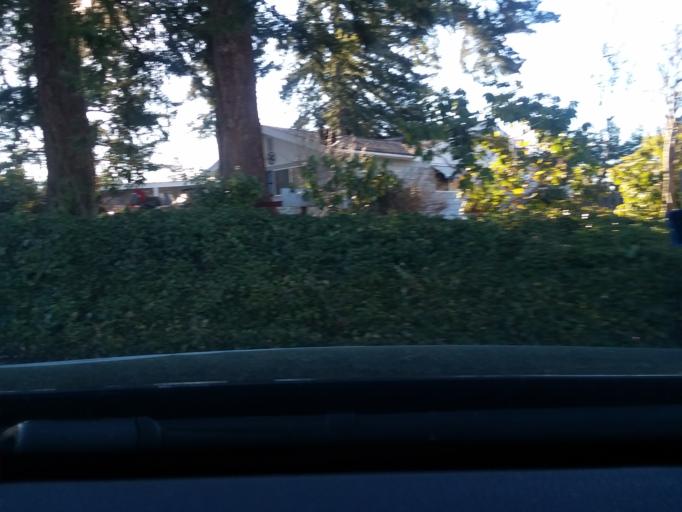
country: US
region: Washington
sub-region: Pierce County
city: Summit
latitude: 47.1304
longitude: -122.3595
